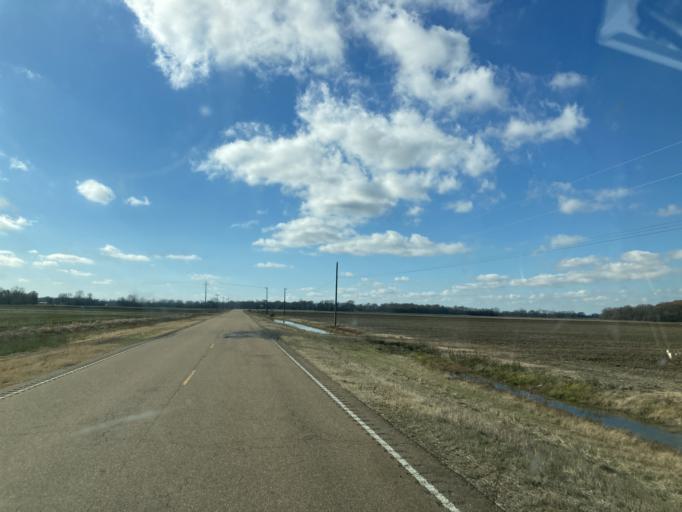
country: US
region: Mississippi
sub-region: Yazoo County
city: Yazoo City
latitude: 32.9625
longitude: -90.4866
